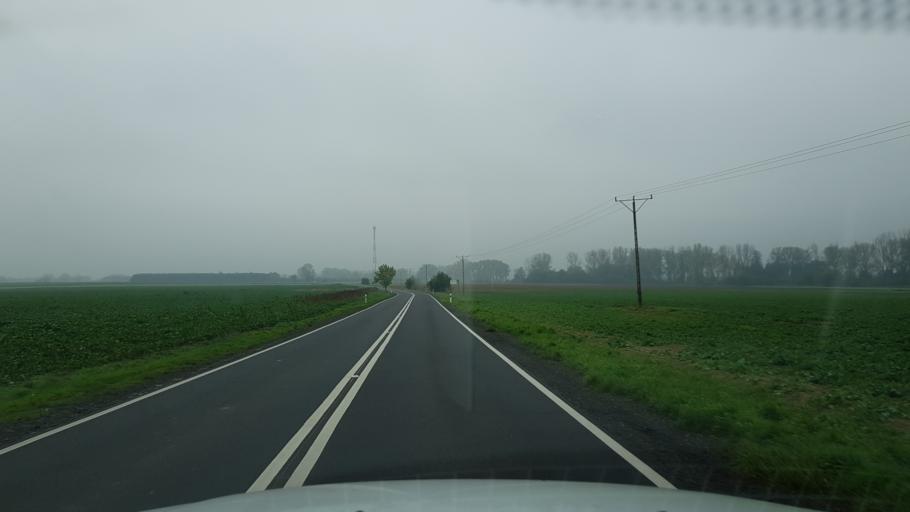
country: PL
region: West Pomeranian Voivodeship
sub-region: Powiat stargardzki
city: Stargard Szczecinski
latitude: 53.2485
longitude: 15.1034
